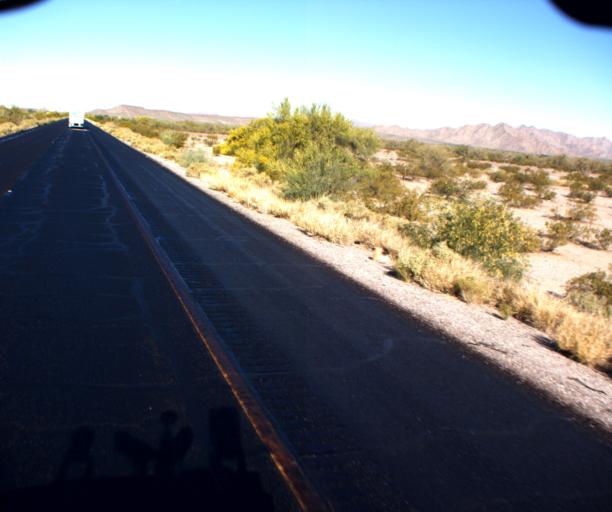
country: US
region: Arizona
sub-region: Pinal County
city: Maricopa
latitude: 32.8444
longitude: -112.2735
